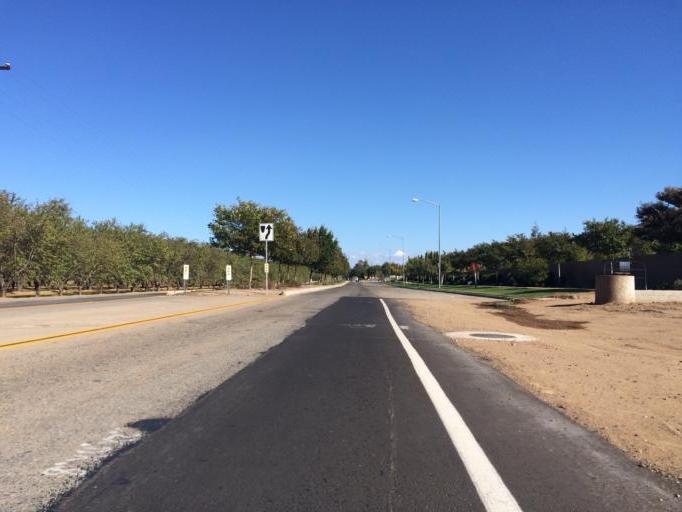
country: US
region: California
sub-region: Fresno County
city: Clovis
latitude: 36.8665
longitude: -119.6976
